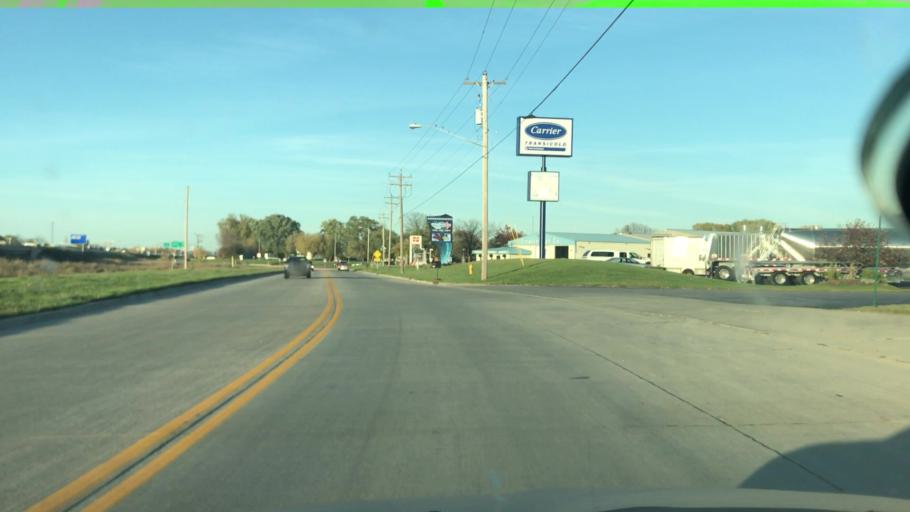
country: US
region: Wisconsin
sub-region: Brown County
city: De Pere
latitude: 44.4428
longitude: -88.0952
